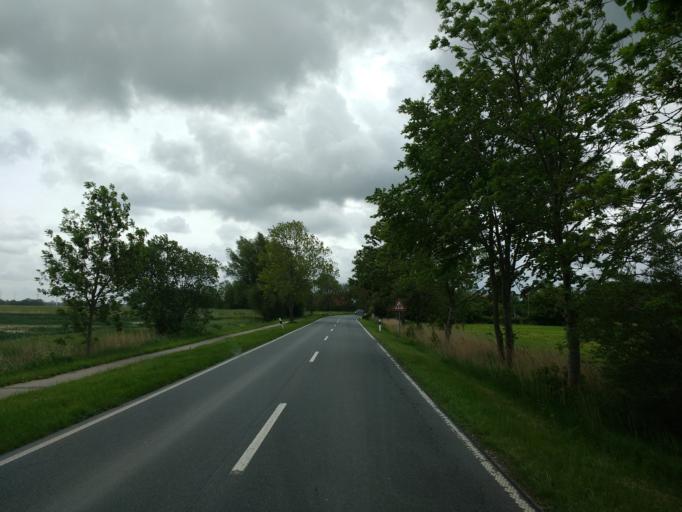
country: DE
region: Lower Saxony
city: Schillig
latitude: 53.6798
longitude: 7.9879
